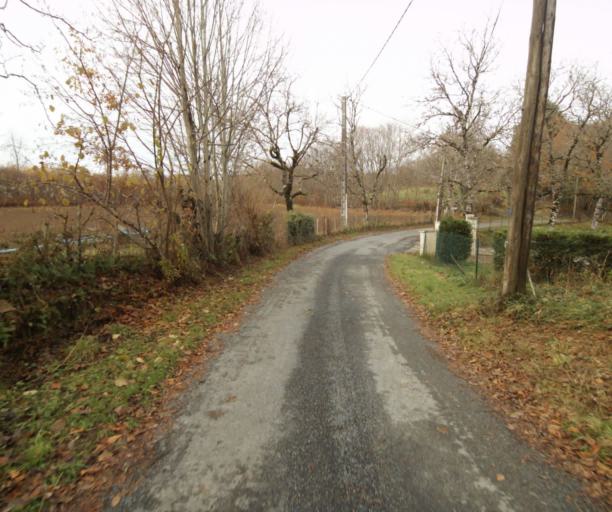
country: FR
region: Limousin
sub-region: Departement de la Correze
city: Sainte-Fortunade
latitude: 45.1808
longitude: 1.7804
